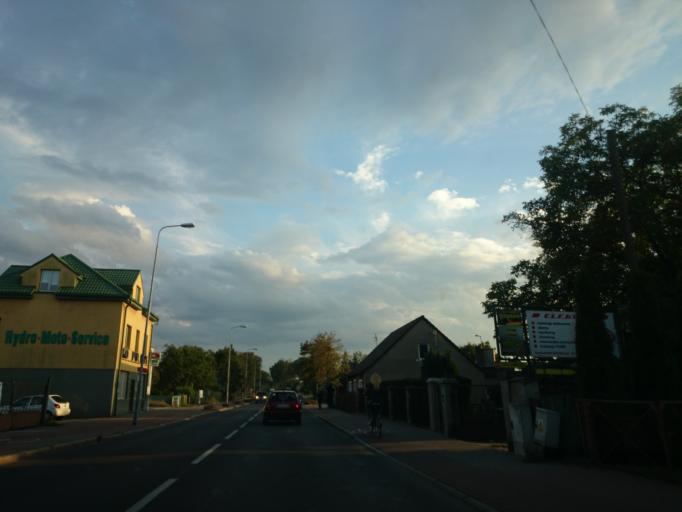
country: PL
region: West Pomeranian Voivodeship
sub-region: Powiat mysliborski
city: Debno
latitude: 52.7341
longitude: 14.6951
